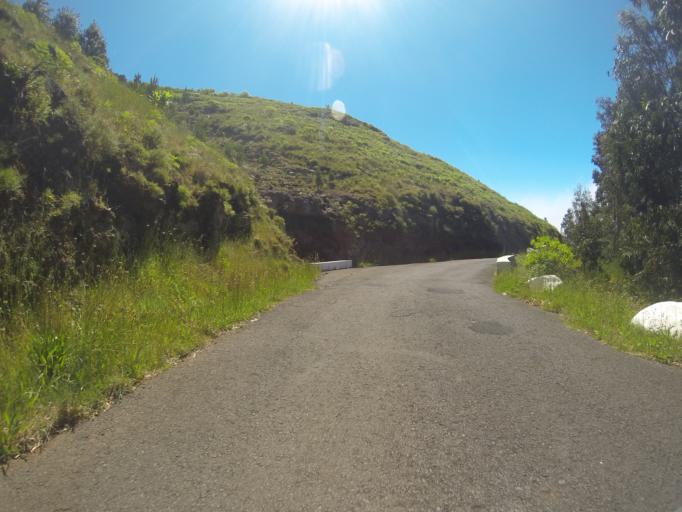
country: PT
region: Madeira
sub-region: Funchal
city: Nossa Senhora do Monte
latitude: 32.7017
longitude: -16.9080
